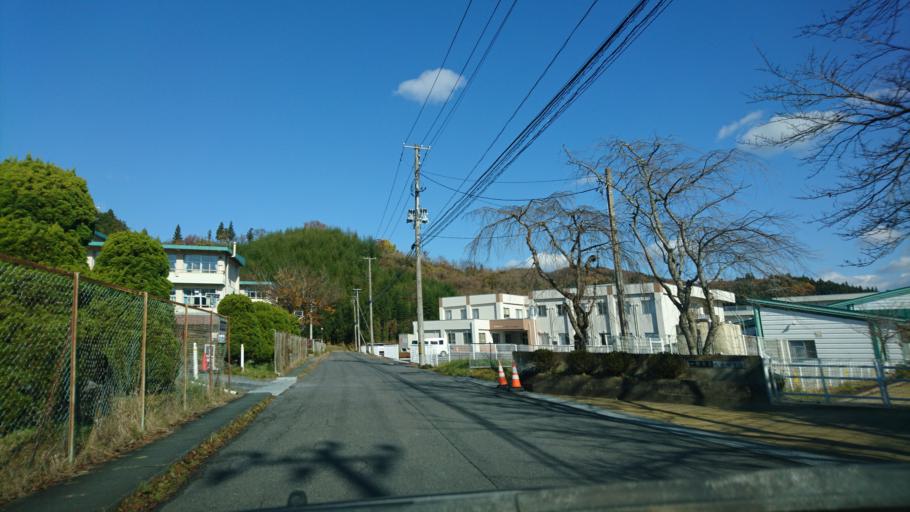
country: JP
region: Iwate
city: Ichinoseki
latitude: 39.0157
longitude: 141.3940
